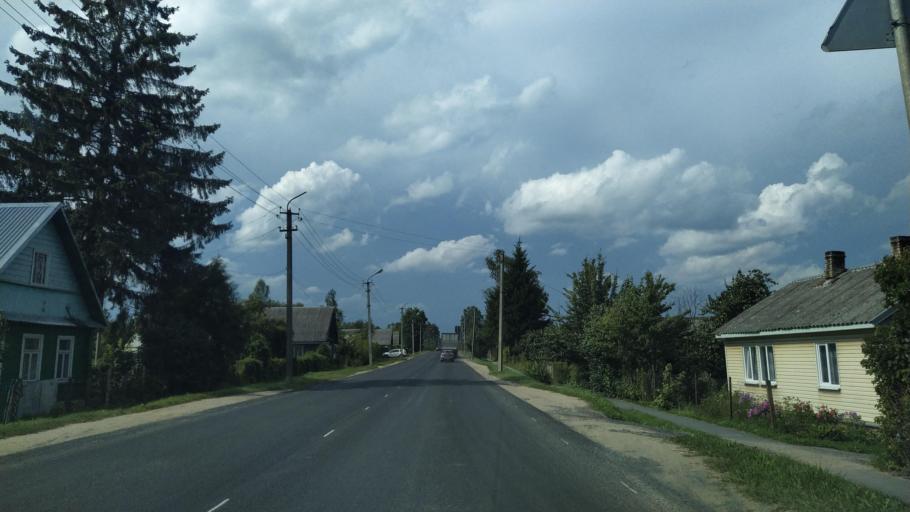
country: RU
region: Pskov
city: Porkhov
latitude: 57.7731
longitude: 29.5492
